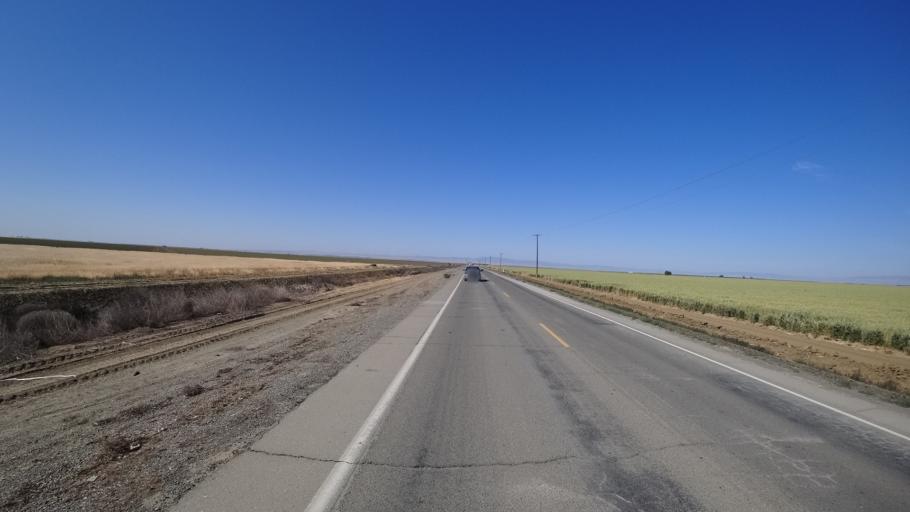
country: US
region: California
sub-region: Kings County
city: Lemoore Station
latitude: 36.2118
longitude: -119.9168
